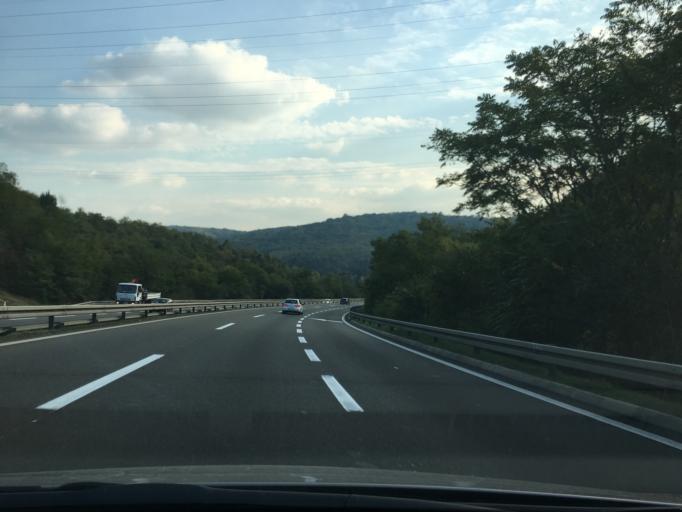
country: RS
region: Central Serbia
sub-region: Belgrade
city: Zvezdara
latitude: 44.7411
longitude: 20.5448
